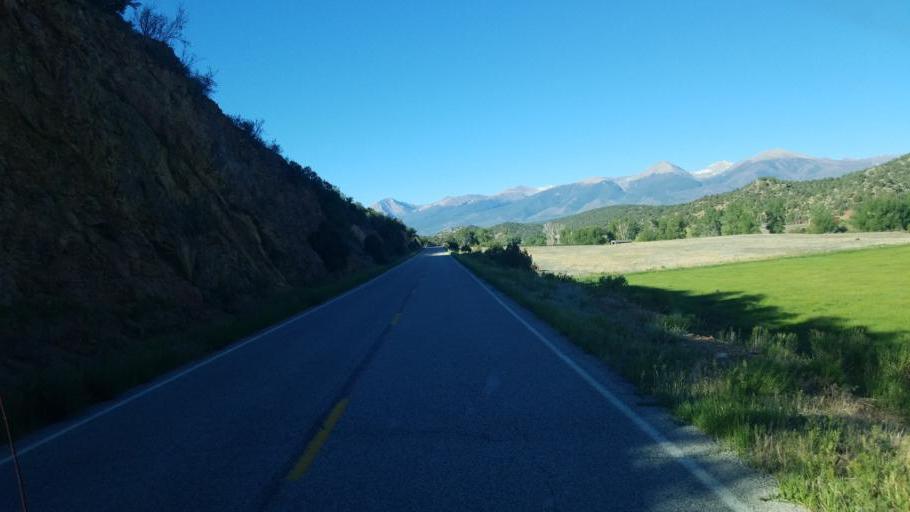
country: US
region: Colorado
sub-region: Custer County
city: Westcliffe
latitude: 38.3616
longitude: -105.5880
